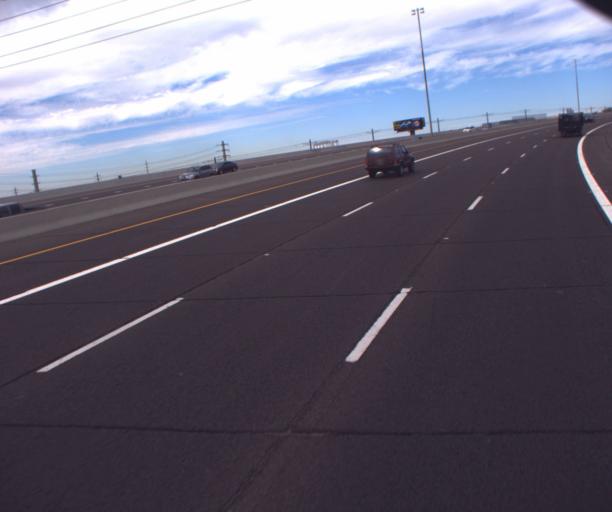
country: US
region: Arizona
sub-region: Maricopa County
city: Tempe Junction
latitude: 33.4405
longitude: -111.9674
